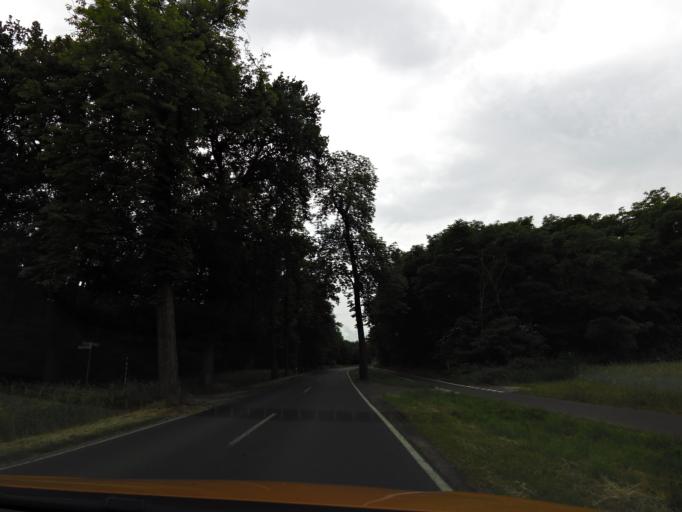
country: DE
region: Brandenburg
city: Rangsdorf
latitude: 52.3096
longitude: 13.3854
